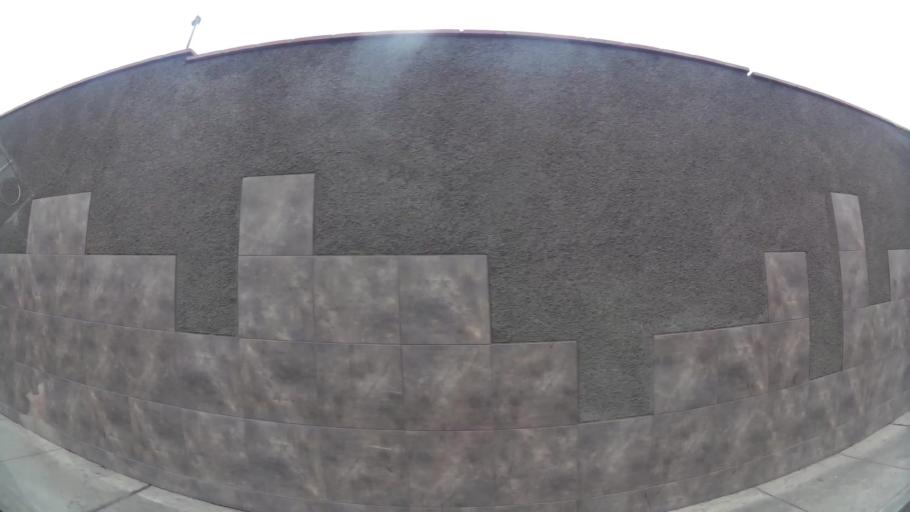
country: PE
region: Lima
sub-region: Lima
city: La Molina
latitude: -12.0808
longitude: -76.9254
